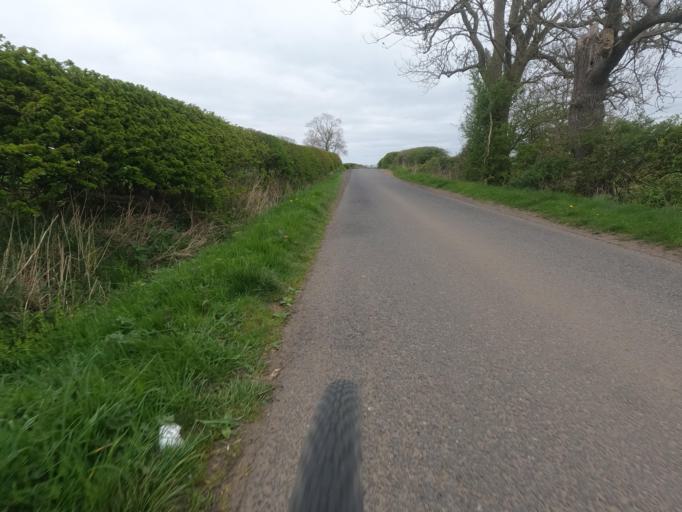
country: GB
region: England
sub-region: Northumberland
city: Darras Hall
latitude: 55.0773
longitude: -1.7901
